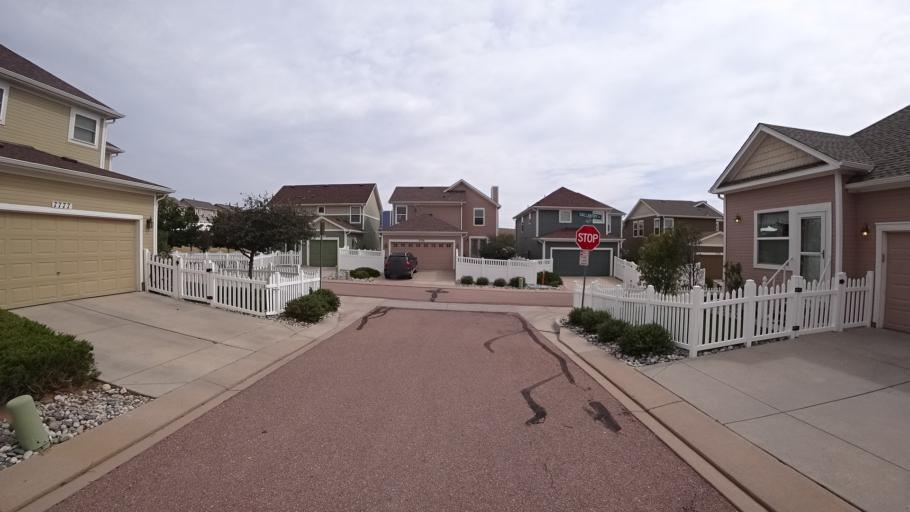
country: US
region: Colorado
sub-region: El Paso County
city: Cimarron Hills
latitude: 38.9154
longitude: -104.6852
